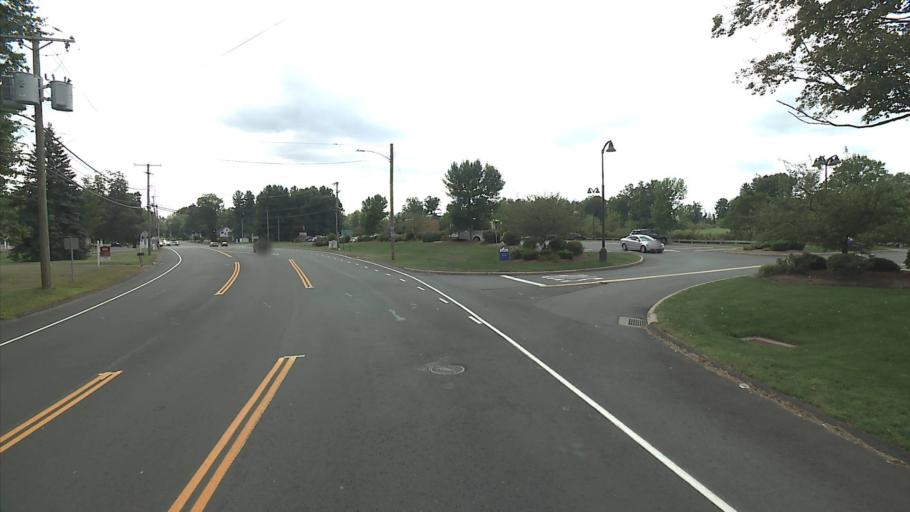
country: US
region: Connecticut
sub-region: Hartford County
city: Blue Hills
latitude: 41.8185
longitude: -72.7393
